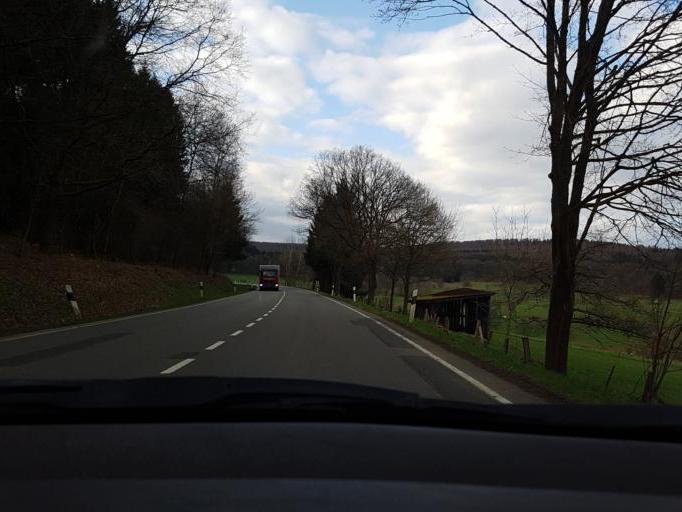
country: DE
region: Lower Saxony
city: Bodenfelde
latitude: 51.7057
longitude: 9.5471
